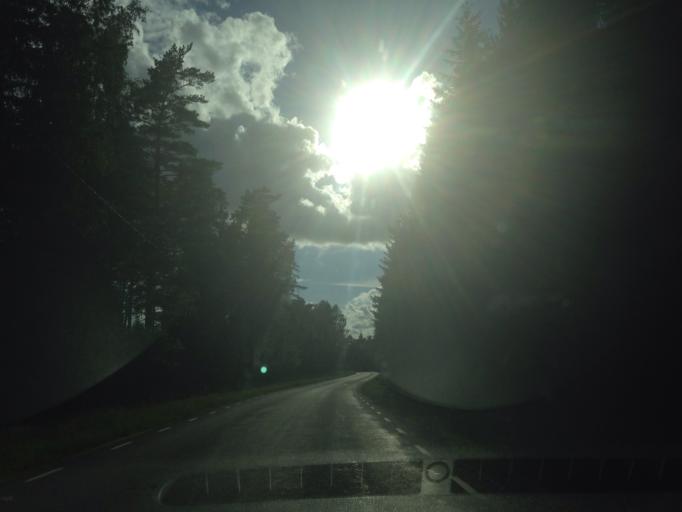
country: SE
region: Vaestra Goetaland
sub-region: Marks Kommun
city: Horred
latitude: 57.4768
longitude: 12.4188
